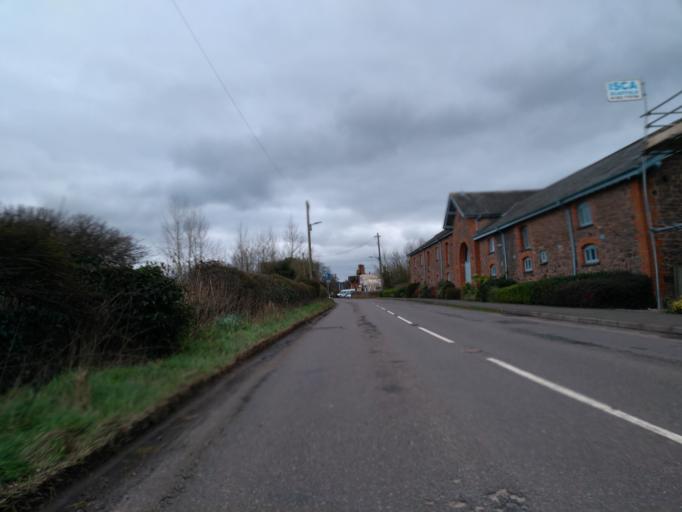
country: GB
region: England
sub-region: Devon
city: Heavitree
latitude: 50.7849
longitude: -3.4962
